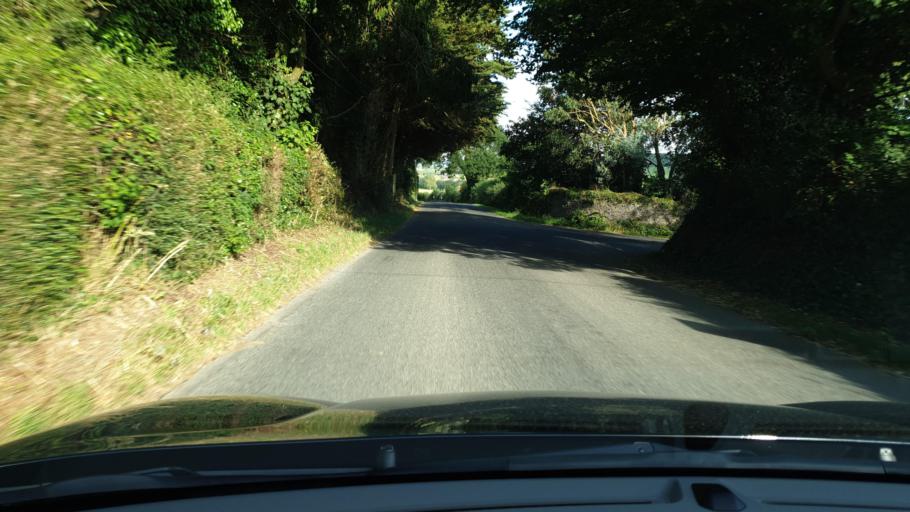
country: IE
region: Leinster
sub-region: An Mhi
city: Stamullin
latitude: 53.6159
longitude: -6.3179
